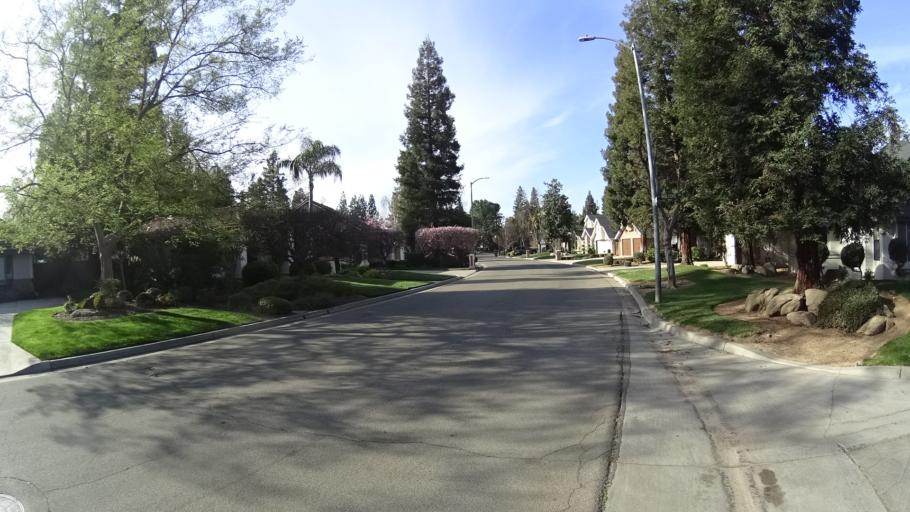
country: US
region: California
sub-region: Fresno County
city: Clovis
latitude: 36.8683
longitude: -119.7745
